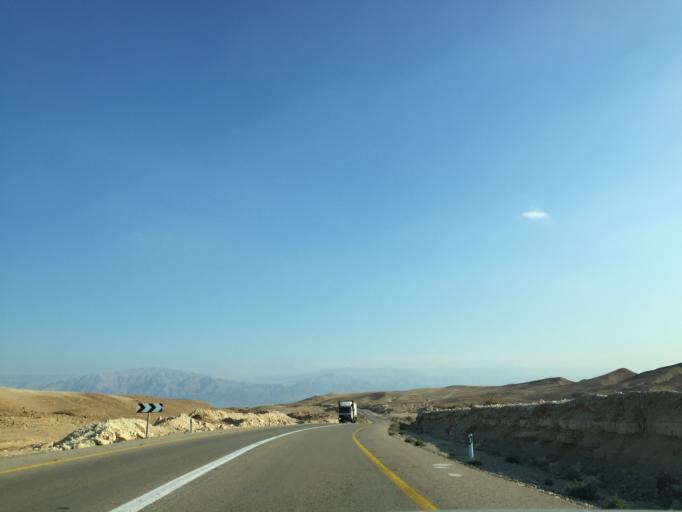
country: IL
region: Southern District
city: `En Boqeq
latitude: 31.1670
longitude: 35.3191
